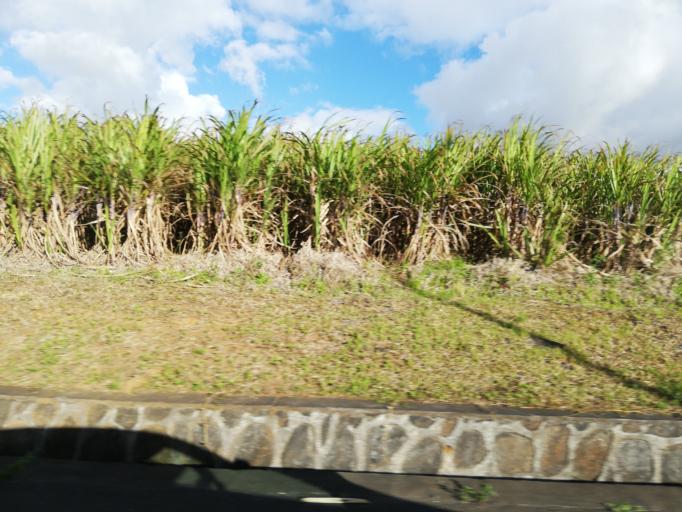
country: MU
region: Moka
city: Quartier Militaire
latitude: -20.2441
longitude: 57.5918
